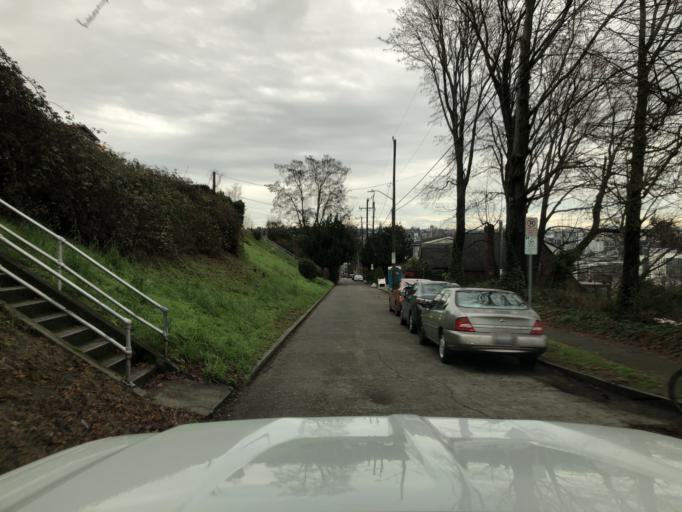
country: US
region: Washington
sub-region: King County
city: Seattle
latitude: 47.6280
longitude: -122.3528
